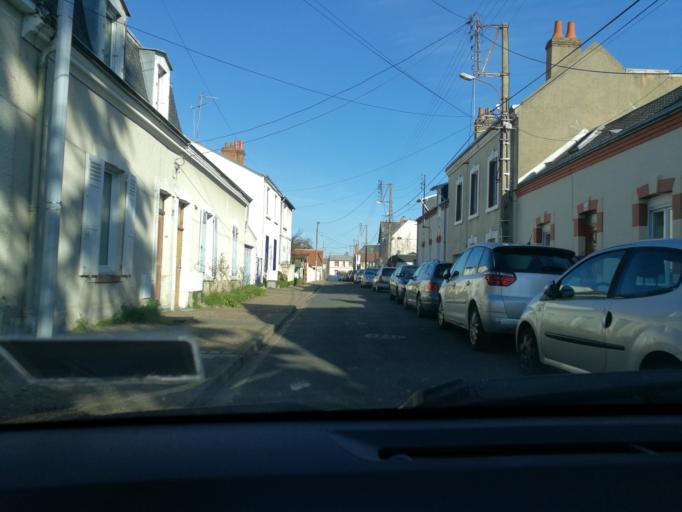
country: FR
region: Centre
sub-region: Departement du Loiret
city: Orleans
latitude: 47.9122
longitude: 1.8912
